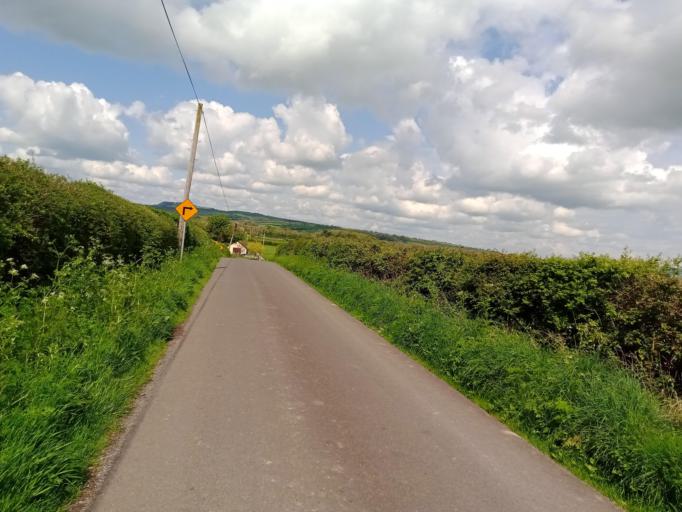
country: IE
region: Leinster
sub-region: Kilkenny
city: Ballyragget
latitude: 52.7318
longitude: -7.4182
